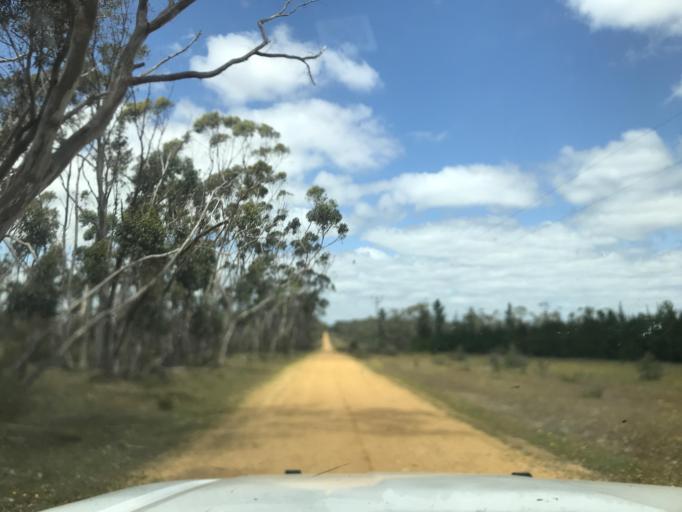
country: AU
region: South Australia
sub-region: Wattle Range
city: Penola
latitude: -37.3670
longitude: 141.1577
